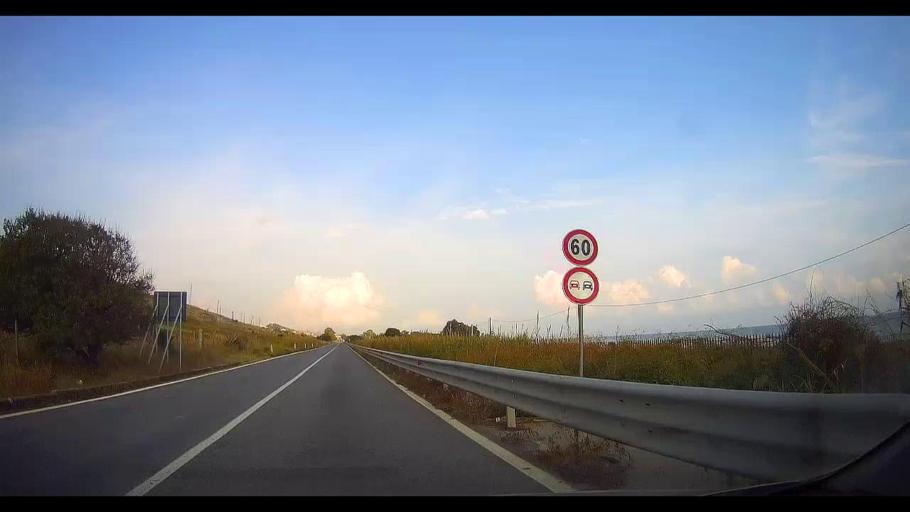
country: IT
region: Calabria
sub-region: Provincia di Cosenza
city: Cariati
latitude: 39.5181
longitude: 16.9087
